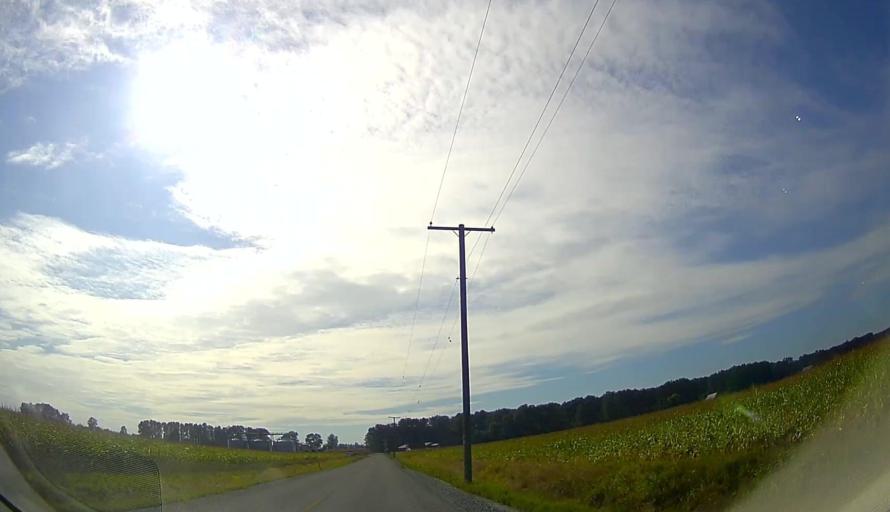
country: US
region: Washington
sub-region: Skagit County
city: Mount Vernon
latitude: 48.3704
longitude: -122.3484
